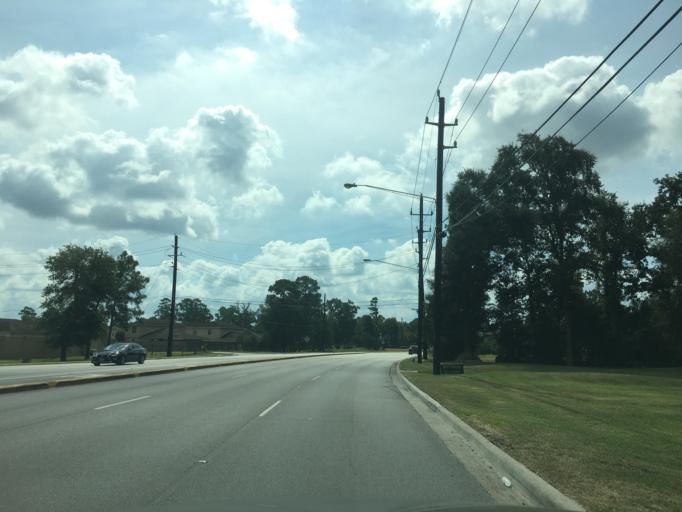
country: US
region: Texas
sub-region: Harris County
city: Spring
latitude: 30.1201
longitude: -95.3985
